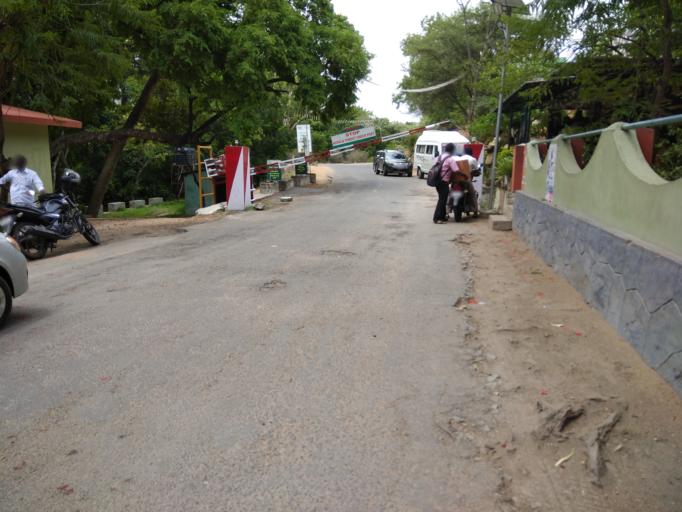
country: IN
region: Tamil Nadu
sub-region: Tiruppur
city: Dhali
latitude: 10.3532
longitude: 77.2204
